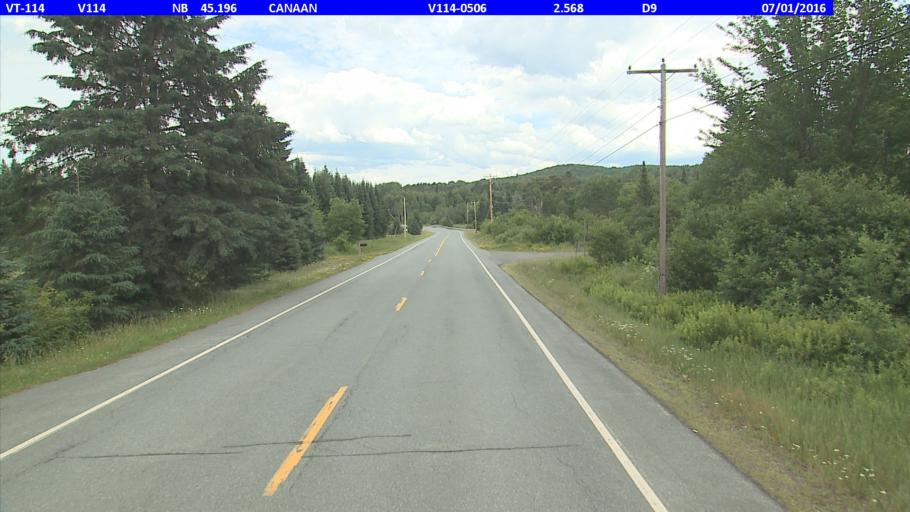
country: US
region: New Hampshire
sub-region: Coos County
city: Colebrook
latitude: 45.0063
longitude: -71.6417
